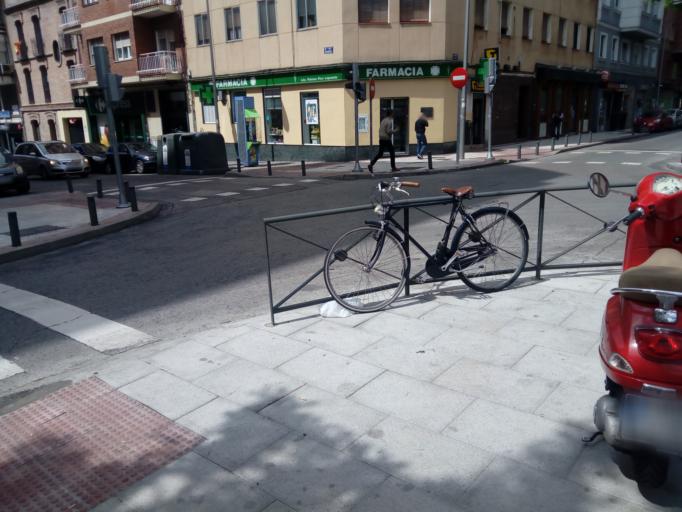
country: ES
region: Madrid
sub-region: Provincia de Madrid
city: Retiro
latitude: 40.4182
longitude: -3.6731
